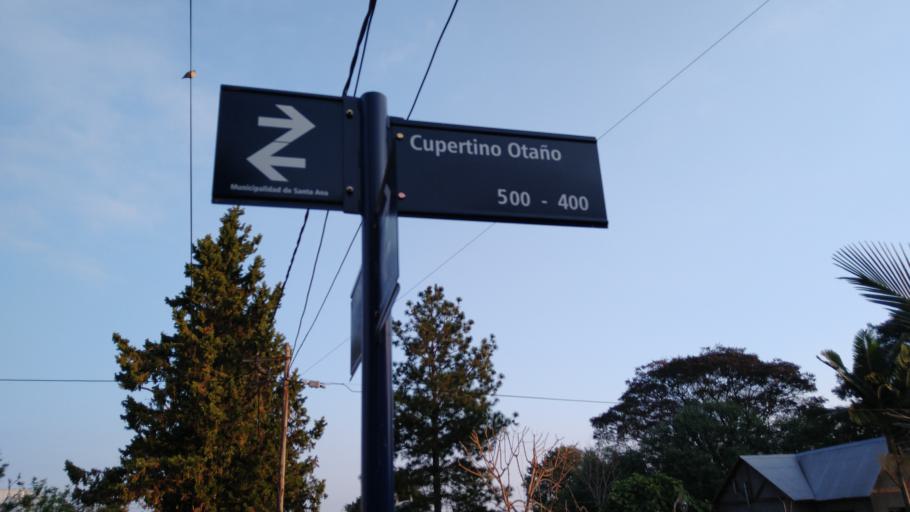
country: AR
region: Entre Rios
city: Santa Ana
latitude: -30.8997
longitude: -57.9318
